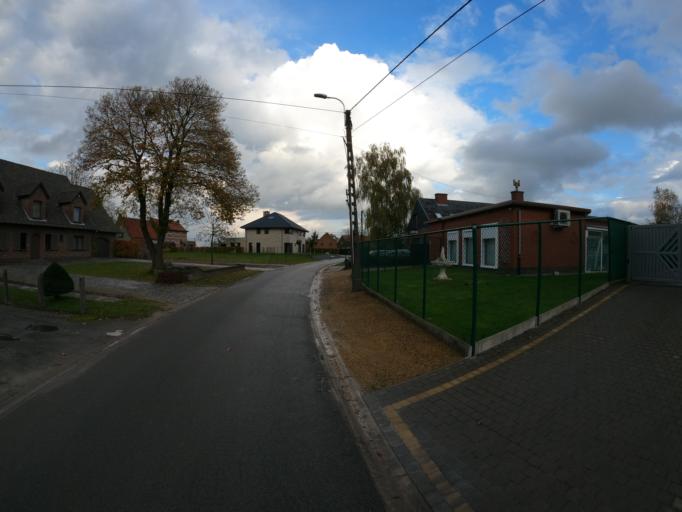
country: BE
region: Flanders
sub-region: Provincie Oost-Vlaanderen
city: Hamme
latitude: 51.1181
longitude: 4.1492
